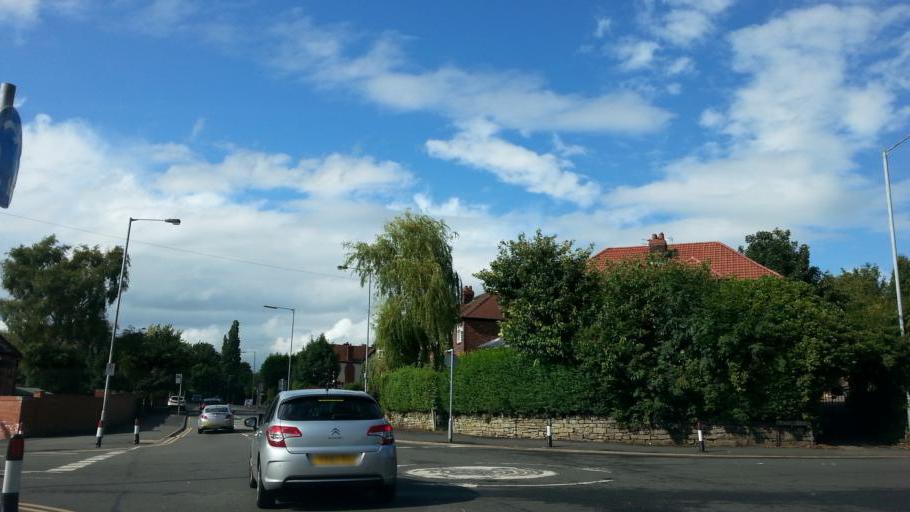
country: GB
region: England
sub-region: Borough of Bury
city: Prestwich
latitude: 53.5285
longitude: -2.2738
